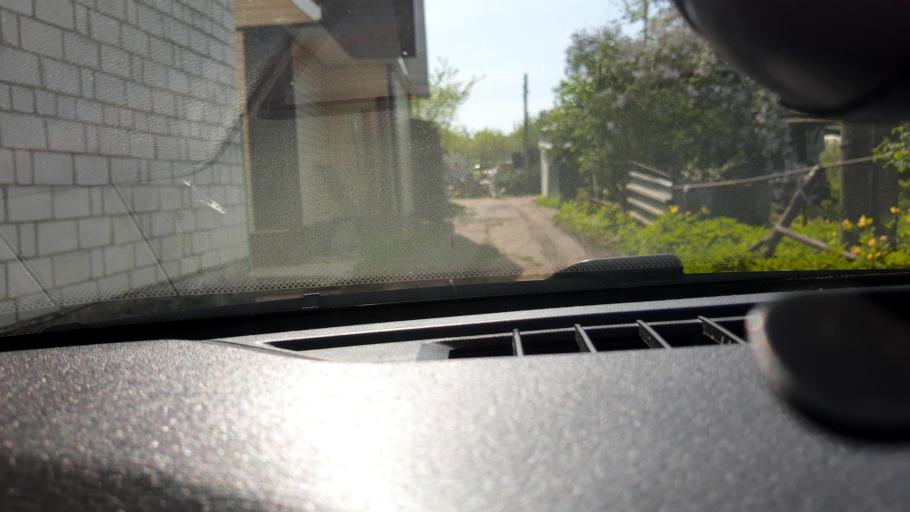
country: RU
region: Nizjnij Novgorod
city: Gorbatovka
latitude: 56.2784
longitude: 43.7868
